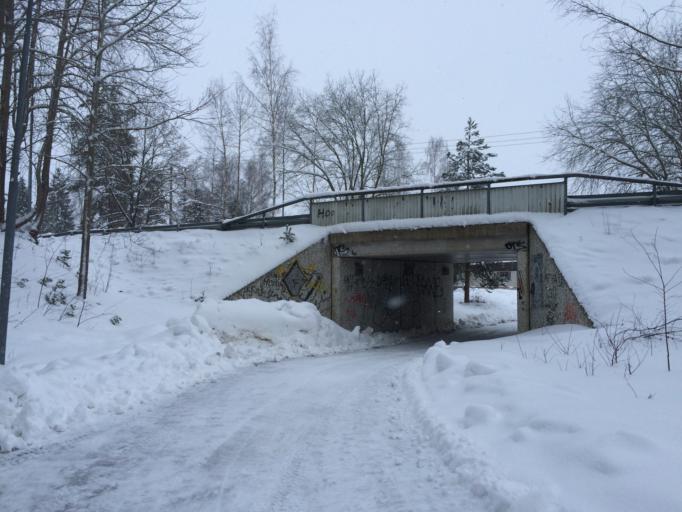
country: SE
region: Vaestmanland
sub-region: Hallstahammars Kommun
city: Hallstahammar
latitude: 59.6248
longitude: 16.2463
